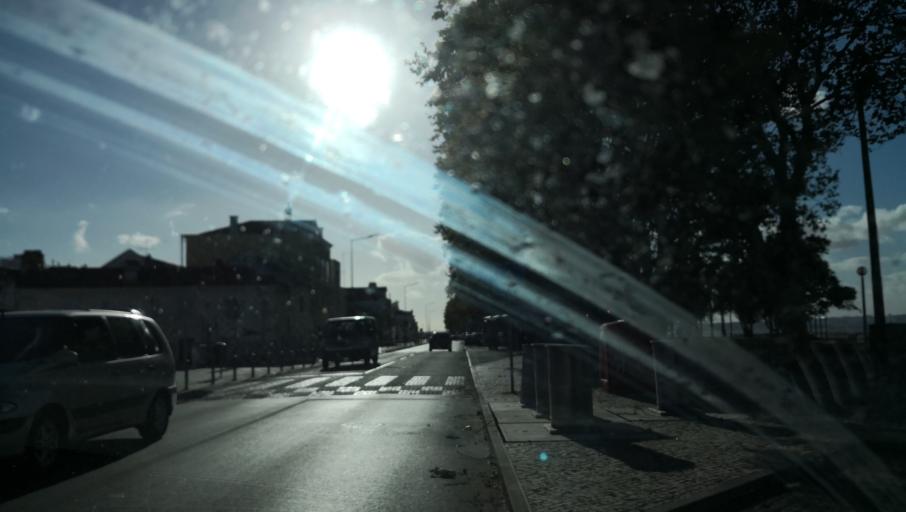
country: PT
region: Setubal
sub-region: Barreiro
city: Barreiro
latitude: 38.6643
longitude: -9.0795
